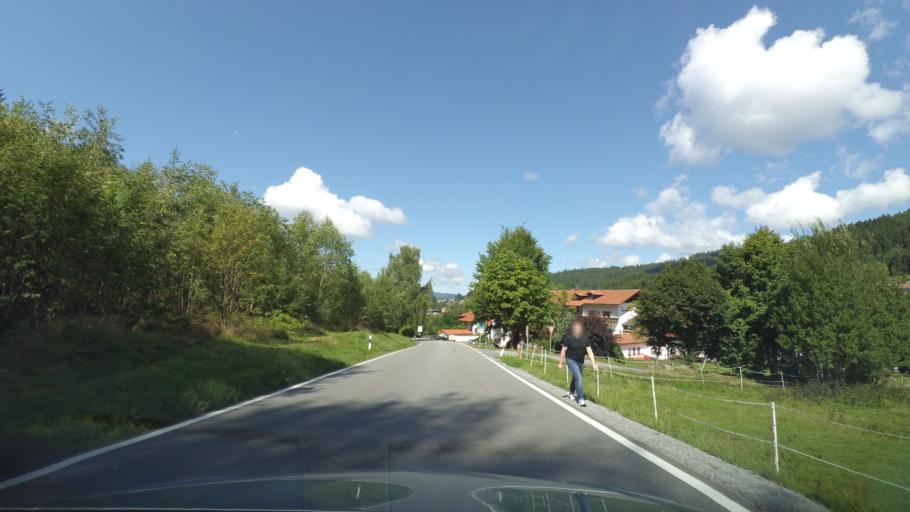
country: DE
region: Bavaria
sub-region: Lower Bavaria
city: Bodenmais
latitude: 49.0670
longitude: 13.1132
